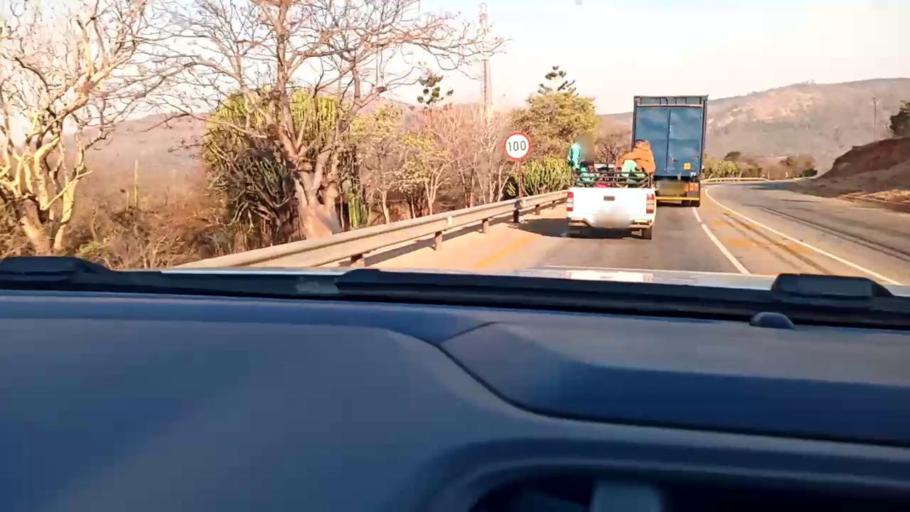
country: ZA
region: Limpopo
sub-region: Mopani District Municipality
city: Ga-Kgapane
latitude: -23.6474
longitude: 30.1705
